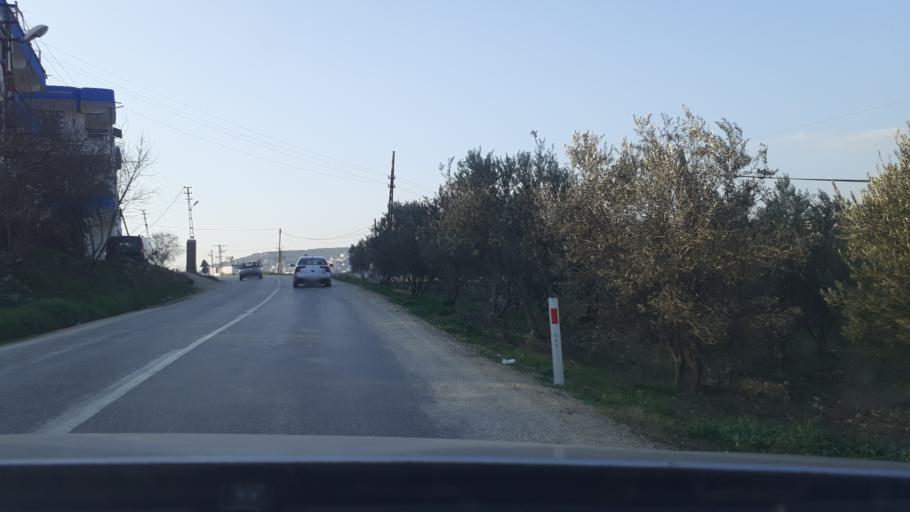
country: TR
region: Hatay
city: Fatikli
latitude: 36.1110
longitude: 36.2654
